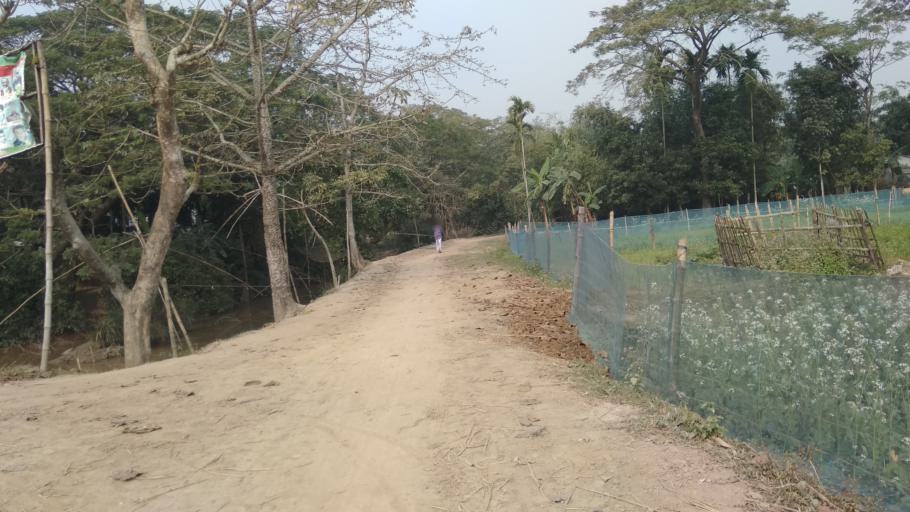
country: BD
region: Dhaka
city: Netrakona
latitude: 24.8908
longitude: 90.6650
